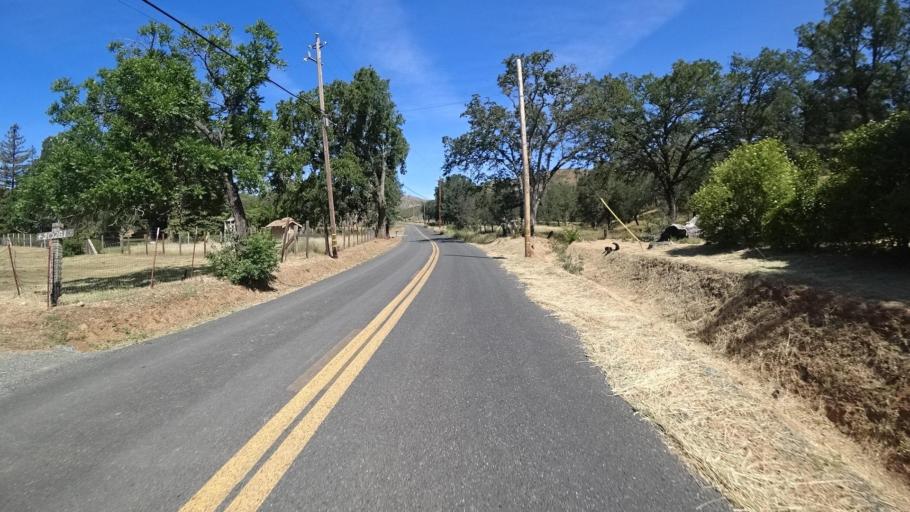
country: US
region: California
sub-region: Lake County
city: Middletown
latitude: 38.7665
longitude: -122.6199
